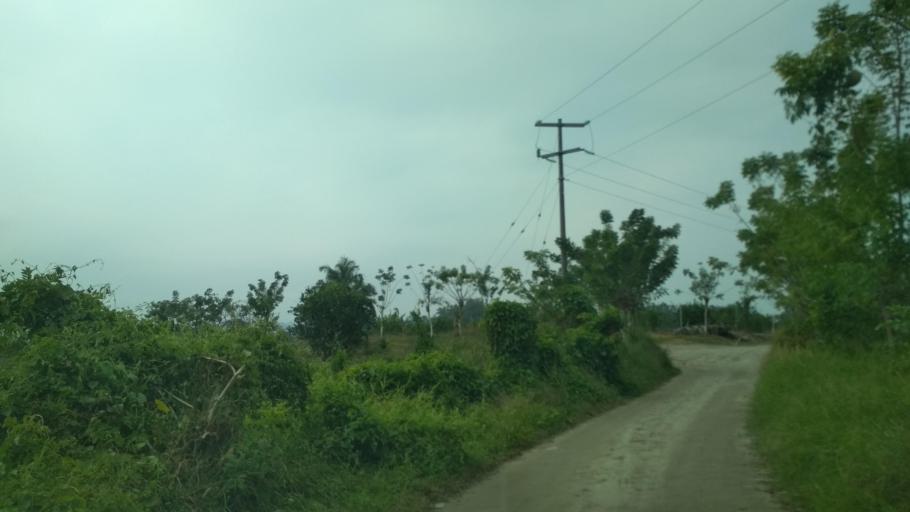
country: MM
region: Kayah
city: Loikaw
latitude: 20.2172
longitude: 97.3325
